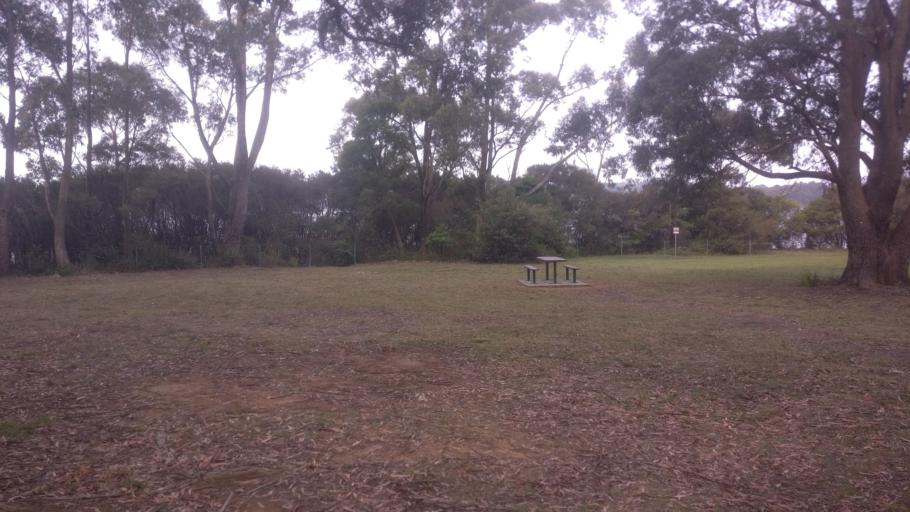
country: AU
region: New South Wales
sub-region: Shoalhaven Shire
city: Kangaroo Valley
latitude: -34.6522
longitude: 150.4908
